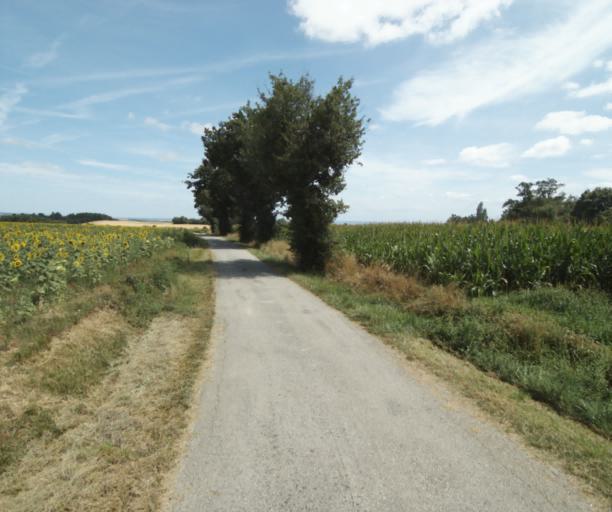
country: FR
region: Midi-Pyrenees
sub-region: Departement du Tarn
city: Soreze
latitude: 43.4819
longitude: 2.0654
